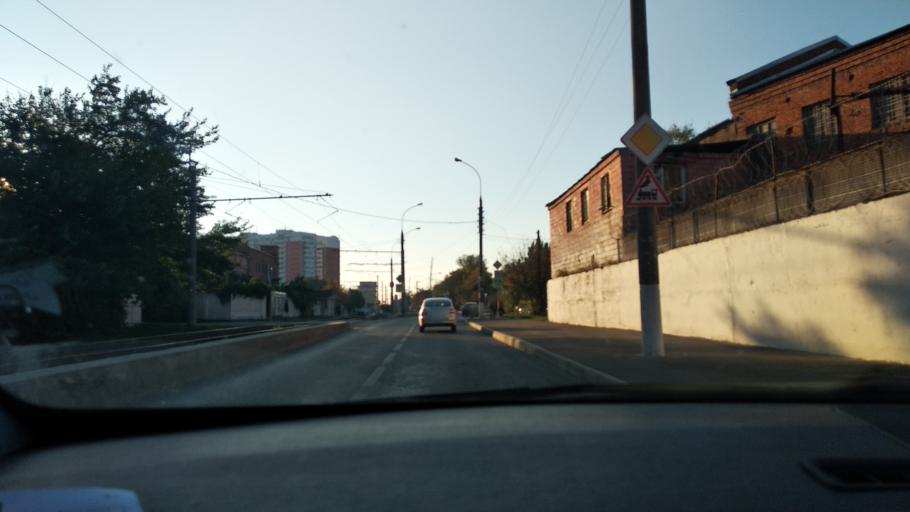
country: RU
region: Krasnodarskiy
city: Krasnodar
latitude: 45.0073
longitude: 39.0160
